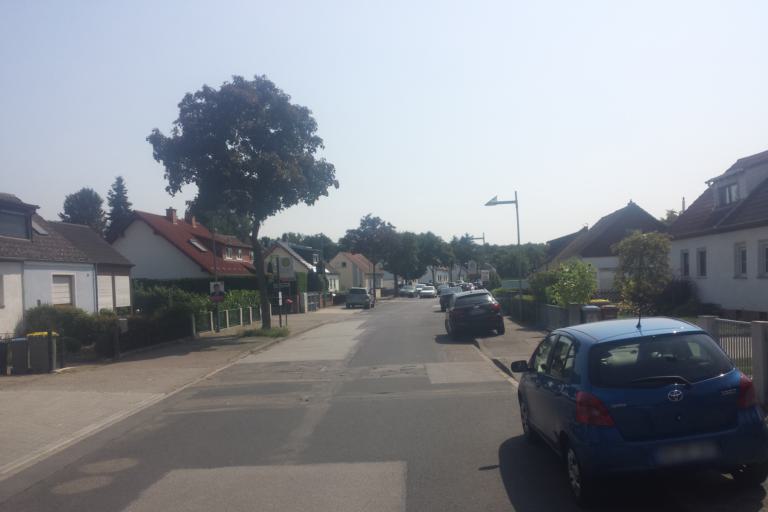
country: DE
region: Baden-Wuerttemberg
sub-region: Karlsruhe Region
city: Mannheim
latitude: 49.5343
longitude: 8.5072
